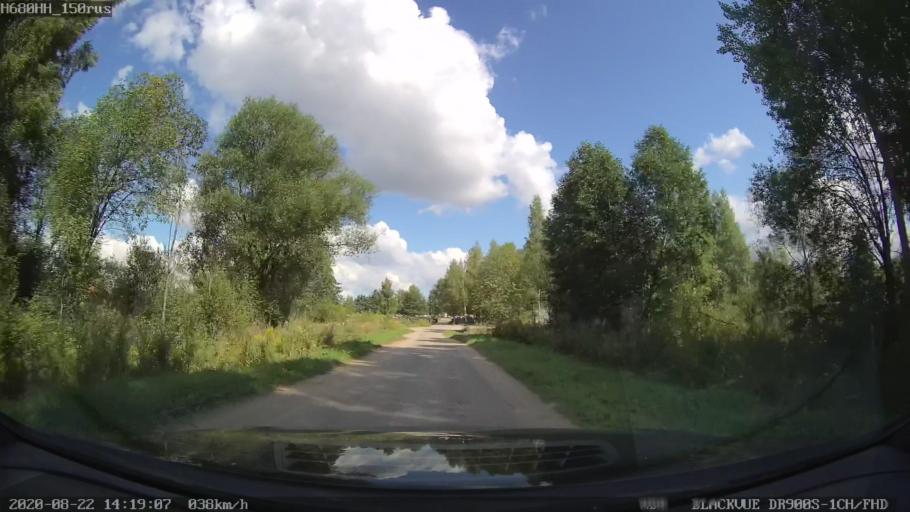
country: RU
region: Tverskaya
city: Bezhetsk
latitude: 57.7596
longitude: 36.7144
